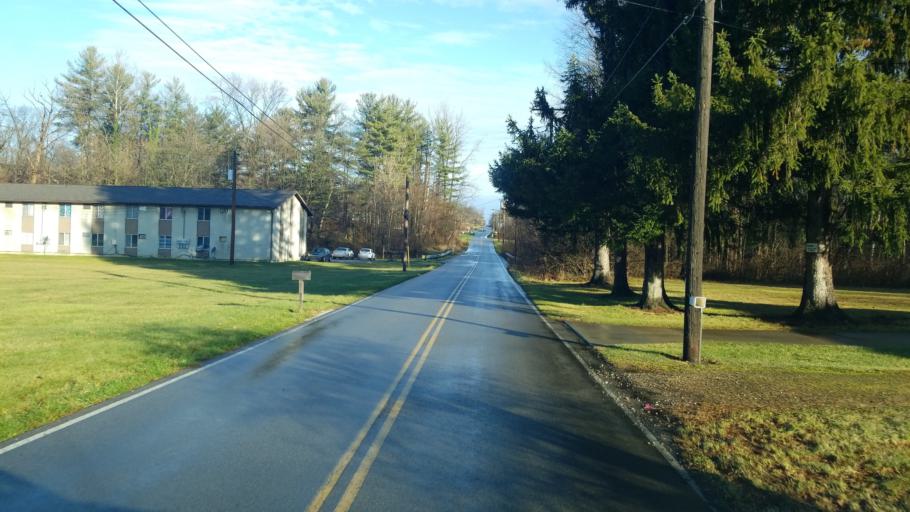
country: US
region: Ohio
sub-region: Richland County
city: Mansfield
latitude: 40.7297
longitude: -82.5036
